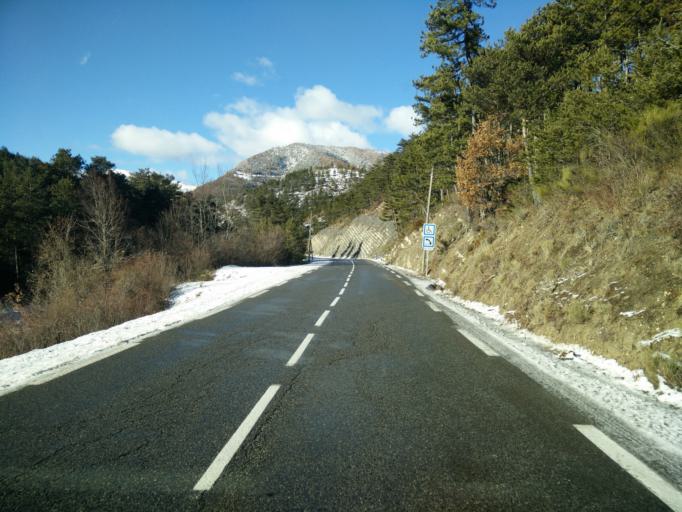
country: FR
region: Provence-Alpes-Cote d'Azur
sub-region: Departement des Alpes-de-Haute-Provence
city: Castellane
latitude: 43.9146
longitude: 6.5676
